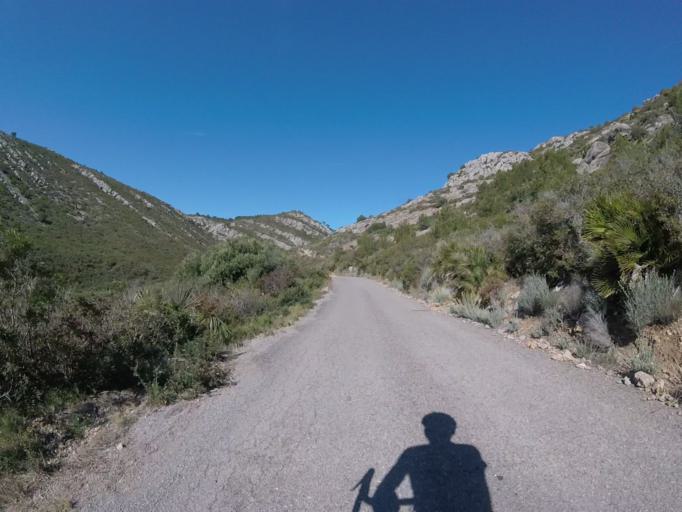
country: ES
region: Valencia
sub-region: Provincia de Castello
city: Orpesa/Oropesa del Mar
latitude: 40.0769
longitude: 0.1075
